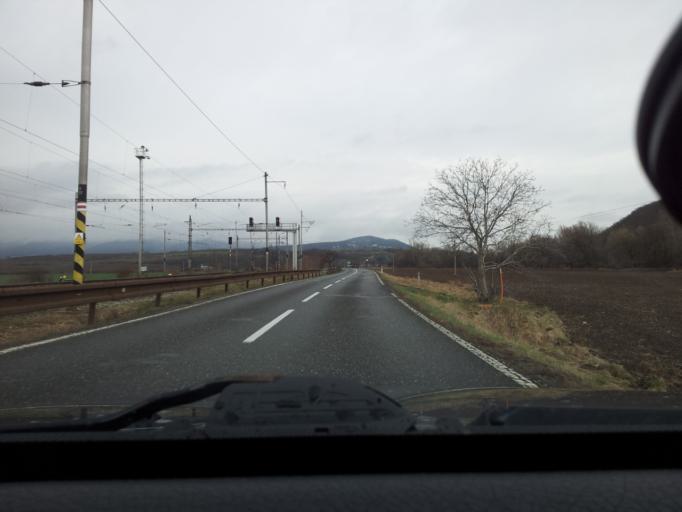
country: SK
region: Nitriansky
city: Tlmace
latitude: 48.3165
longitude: 18.5391
